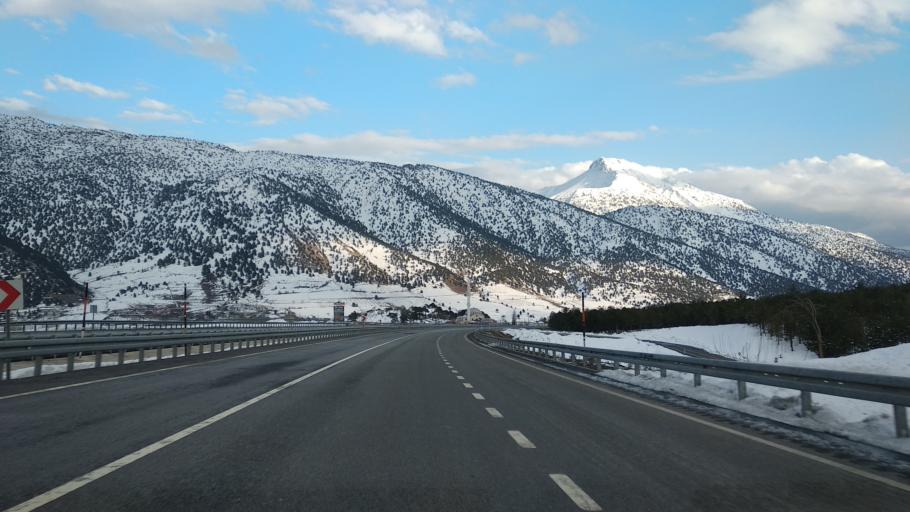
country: TR
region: Kahramanmaras
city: Goksun
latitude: 37.9046
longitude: 36.6062
